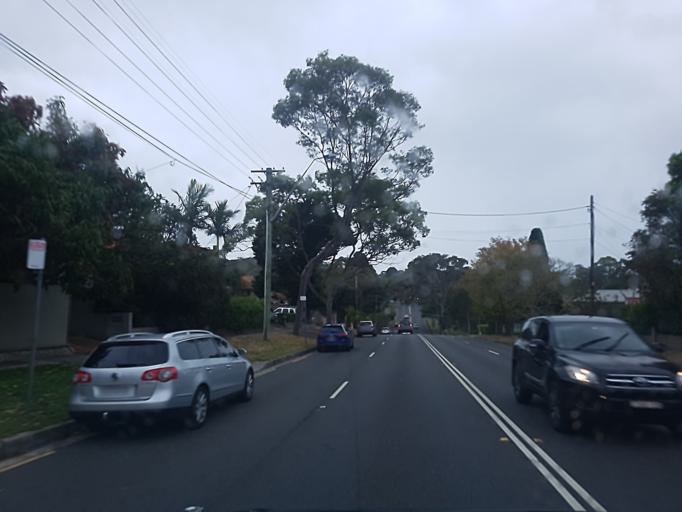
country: AU
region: New South Wales
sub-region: Willoughby
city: Castlecrag
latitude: -33.8002
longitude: 151.2109
